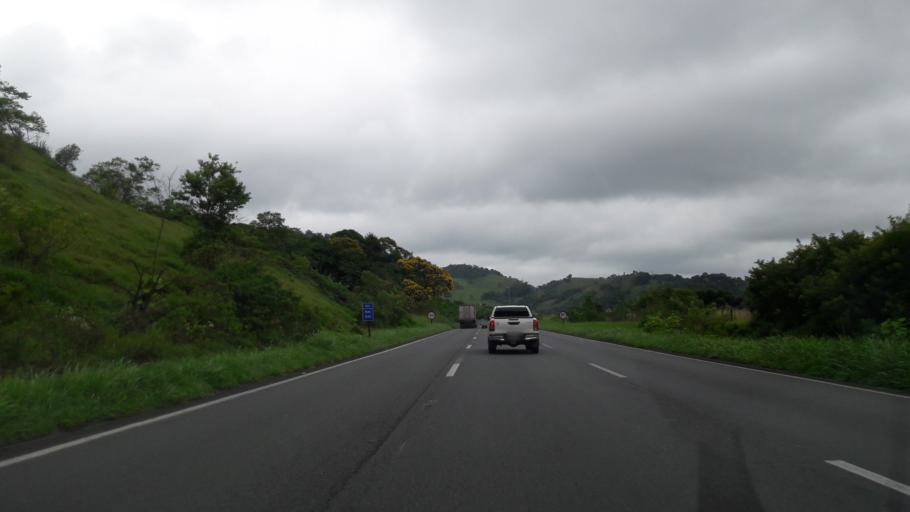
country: BR
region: Sao Paulo
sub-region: Cajati
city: Cajati
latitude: -24.9622
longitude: -48.4689
